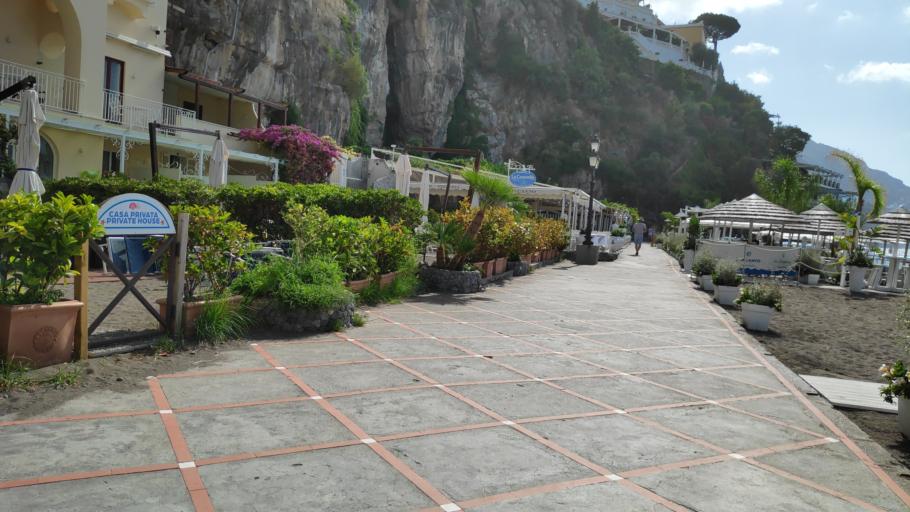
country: IT
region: Campania
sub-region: Provincia di Salerno
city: Positano
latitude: 40.6278
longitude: 14.4880
